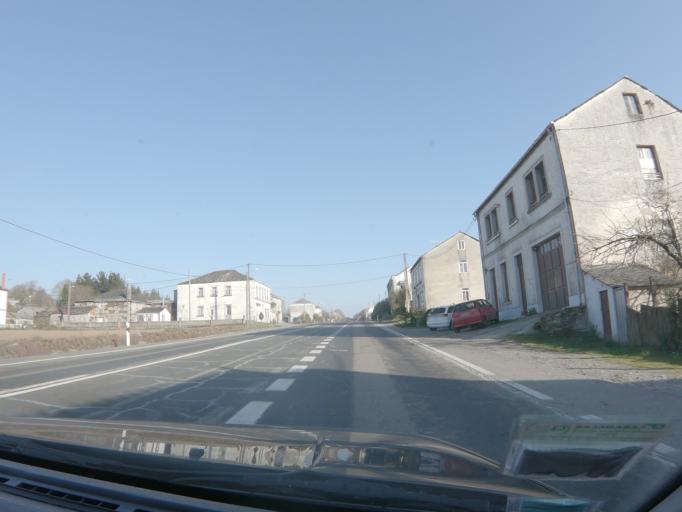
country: ES
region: Galicia
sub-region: Provincia de Lugo
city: Corgo
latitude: 42.9586
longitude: -7.4734
